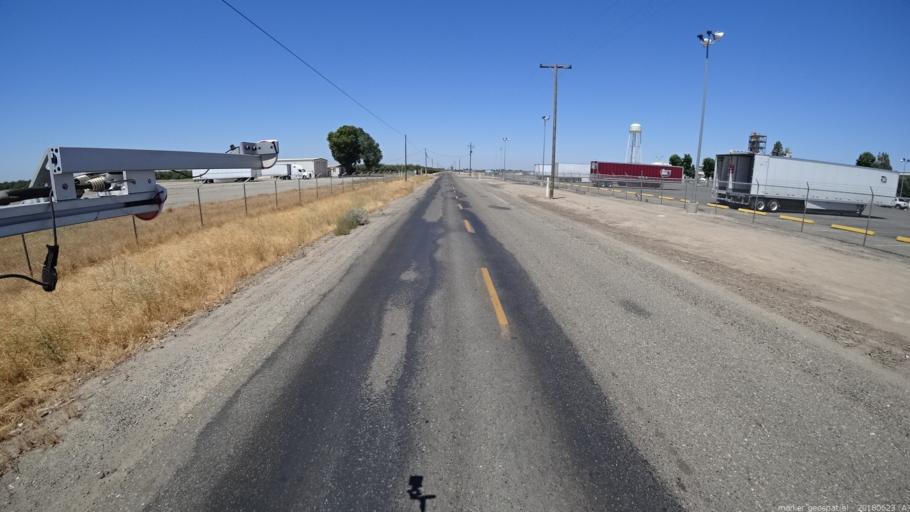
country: US
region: California
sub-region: Madera County
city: Fairmead
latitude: 37.0910
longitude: -120.2234
